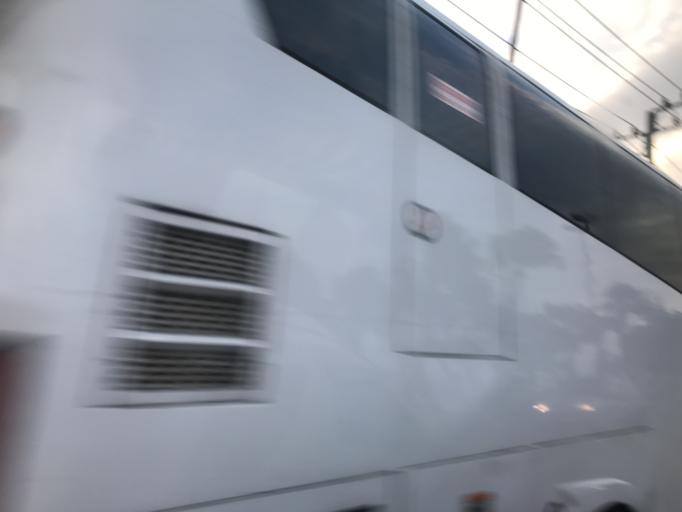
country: TH
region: Chon Buri
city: Phatthaya
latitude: 12.8980
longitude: 100.8677
